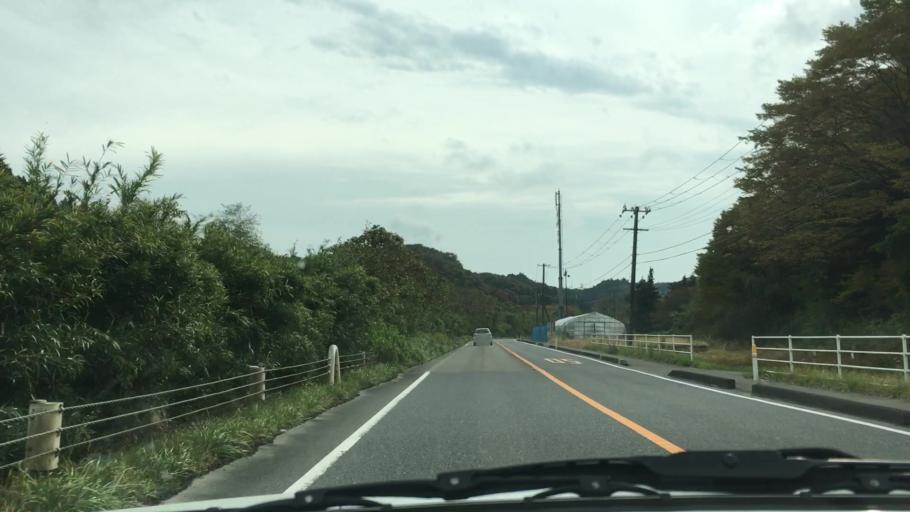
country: JP
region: Miyagi
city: Matsushima
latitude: 38.4282
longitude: 141.0606
